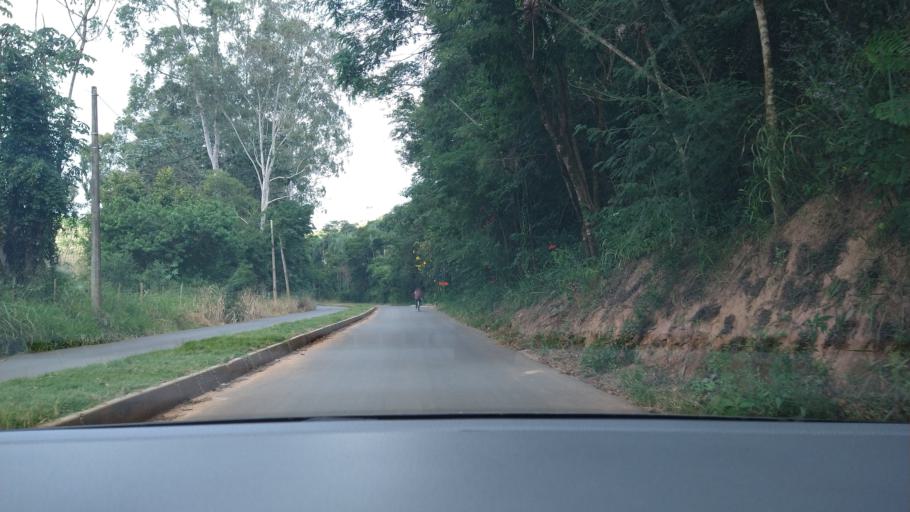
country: BR
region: Minas Gerais
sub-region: Vicosa
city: Vicosa
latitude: -20.7800
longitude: -42.8519
